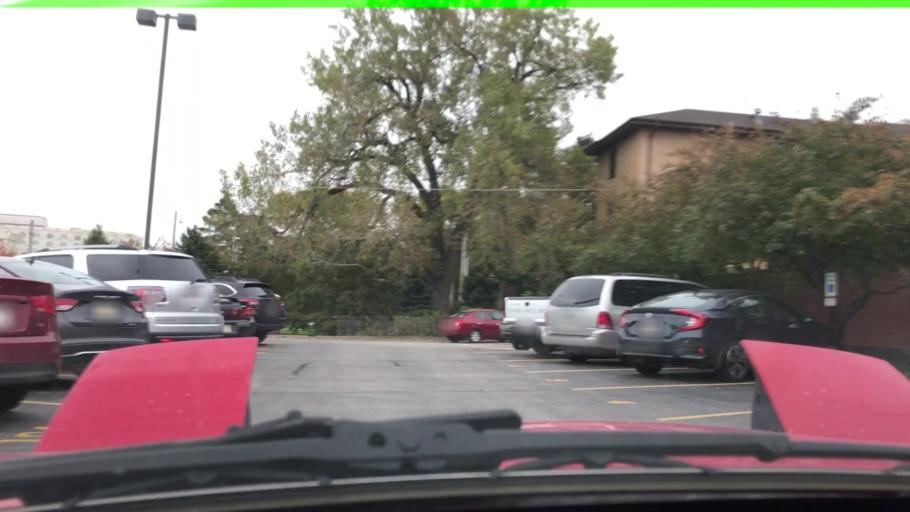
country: US
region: Nebraska
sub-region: Lancaster County
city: Lincoln
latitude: 40.8207
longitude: -96.6992
